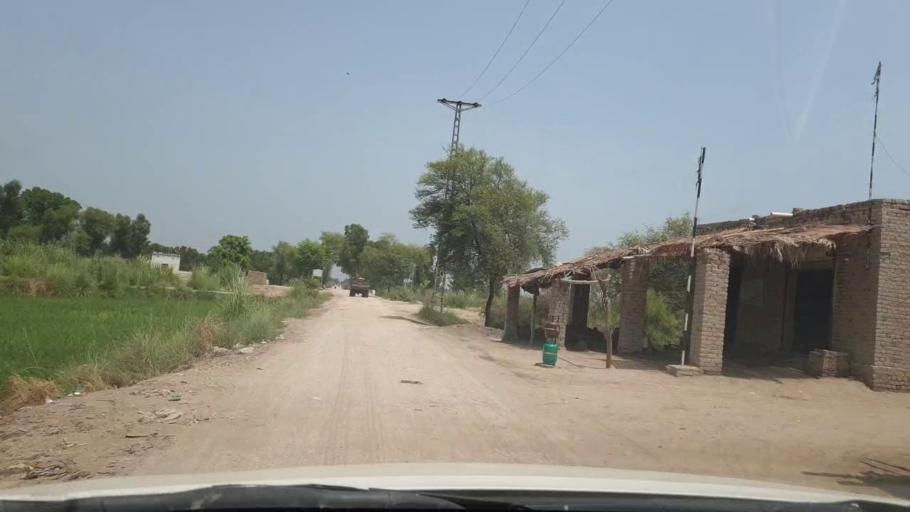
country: PK
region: Sindh
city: Rustam jo Goth
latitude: 28.0229
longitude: 68.8126
